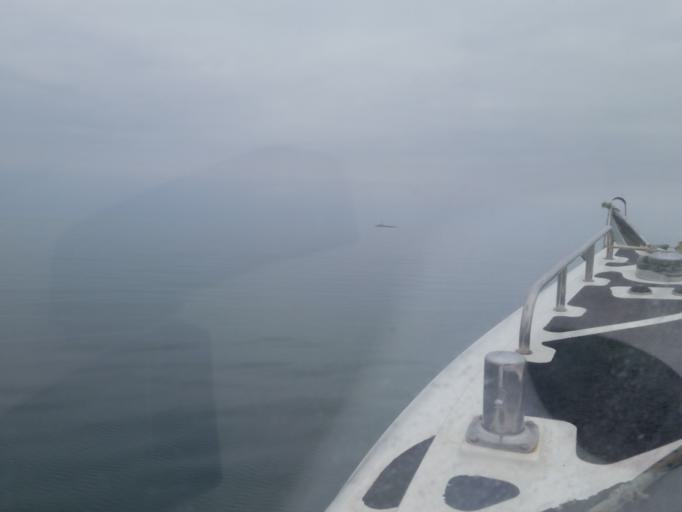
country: IE
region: Leinster
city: An Ros
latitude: 53.5429
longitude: -6.0044
